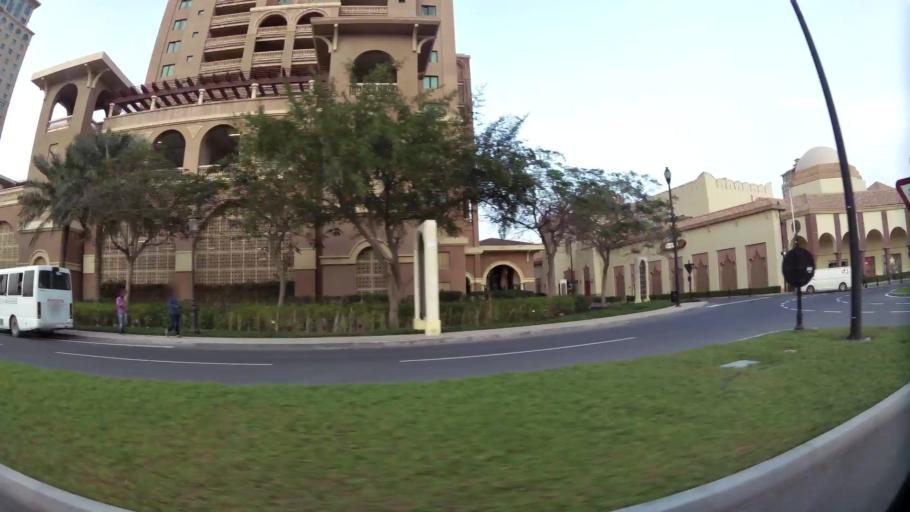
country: QA
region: Baladiyat ad Dawhah
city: Doha
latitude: 25.3655
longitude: 51.5396
